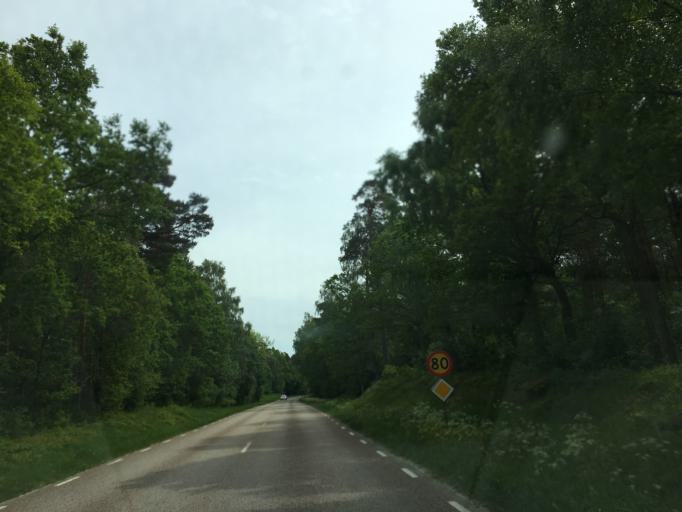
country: SE
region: Skane
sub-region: Sjobo Kommun
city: Blentarp
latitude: 55.6192
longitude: 13.5498
